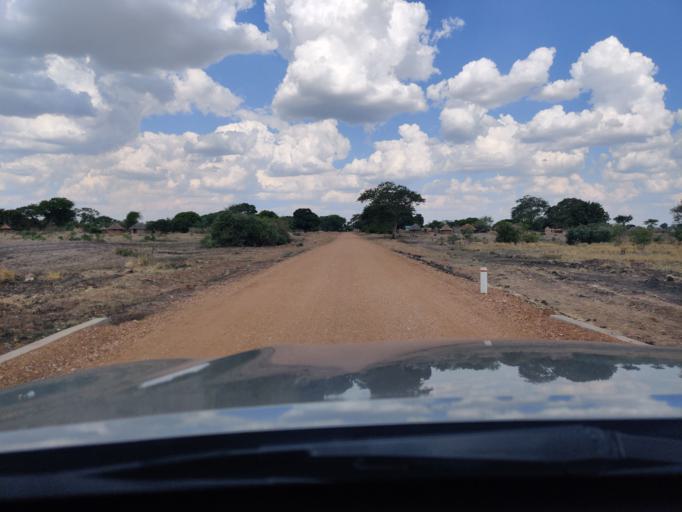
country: ZM
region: Central
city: Chibombo
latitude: -14.7616
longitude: 27.8931
